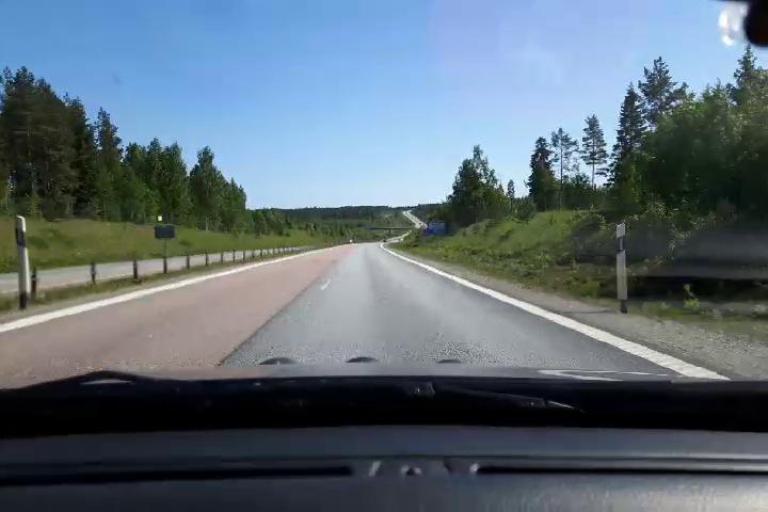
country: SE
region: Gaevleborg
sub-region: Soderhamns Kommun
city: Soderhamn
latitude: 61.3635
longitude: 17.0125
